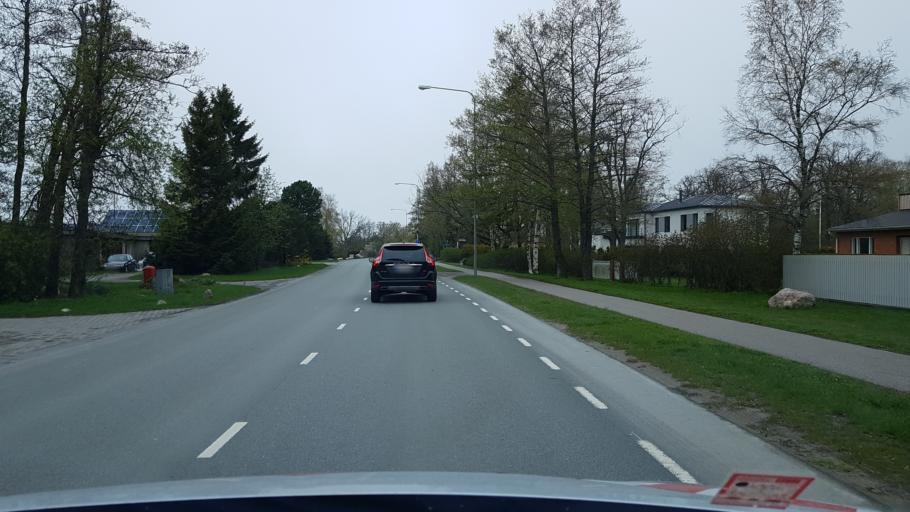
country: EE
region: Harju
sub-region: Viimsi vald
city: Rummu
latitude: 59.5279
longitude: 24.7974
